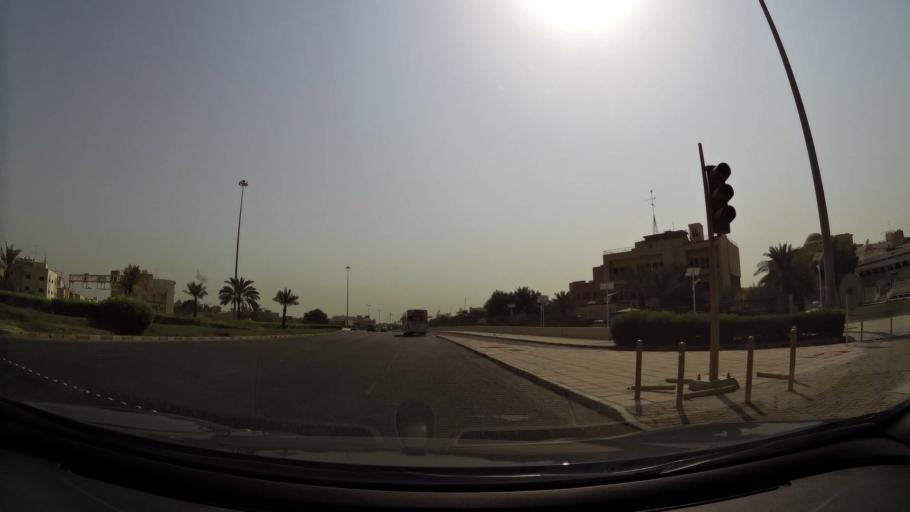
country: KW
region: Al Asimah
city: Ad Dasmah
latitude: 29.3644
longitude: 47.9924
